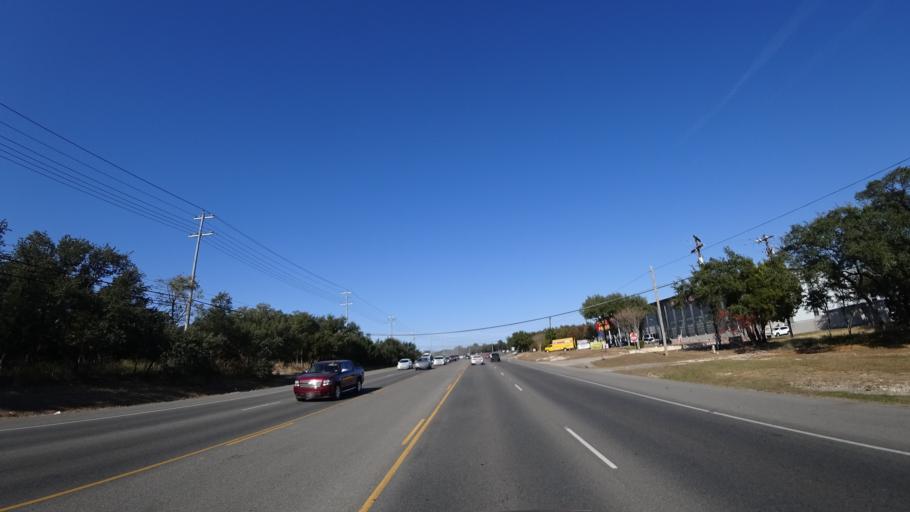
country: US
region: Texas
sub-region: Williamson County
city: Anderson Mill
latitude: 30.4327
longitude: -97.8413
